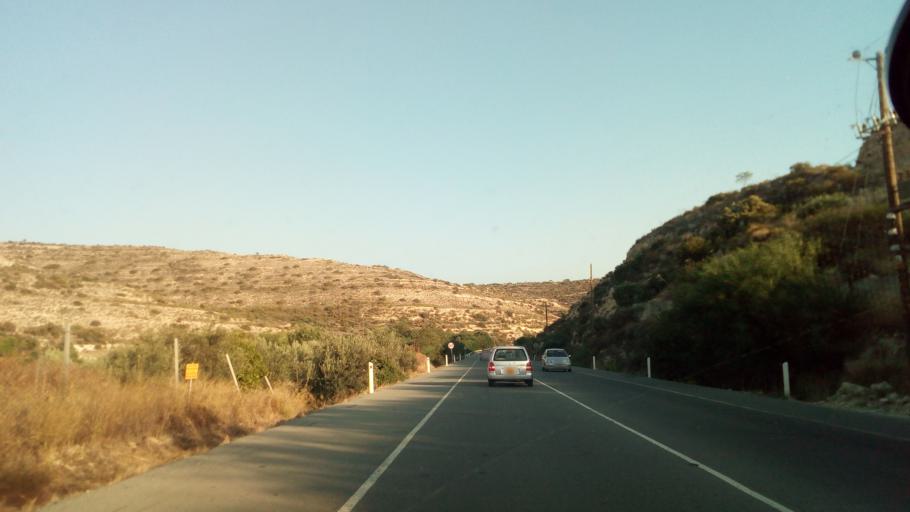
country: CY
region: Limassol
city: Pano Polemidia
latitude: 34.7355
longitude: 32.9870
